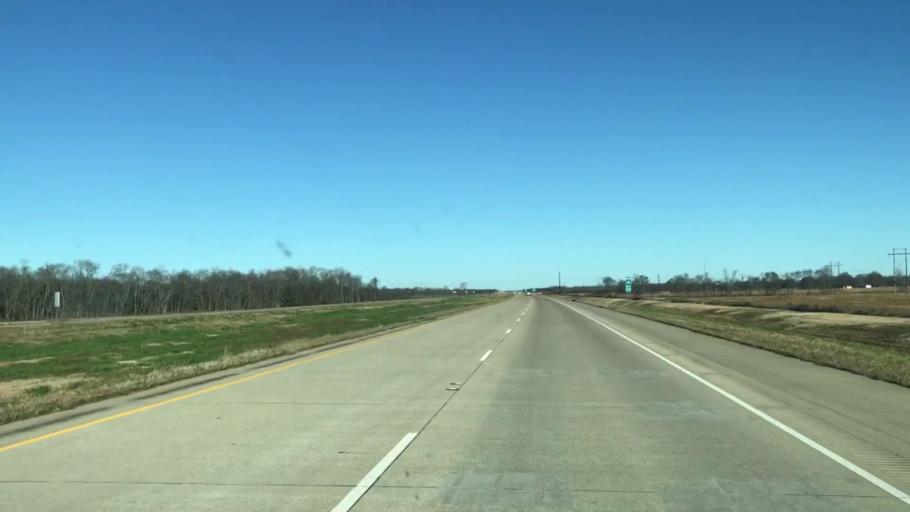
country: US
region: Louisiana
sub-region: Caddo Parish
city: Blanchard
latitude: 32.6564
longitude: -93.8424
